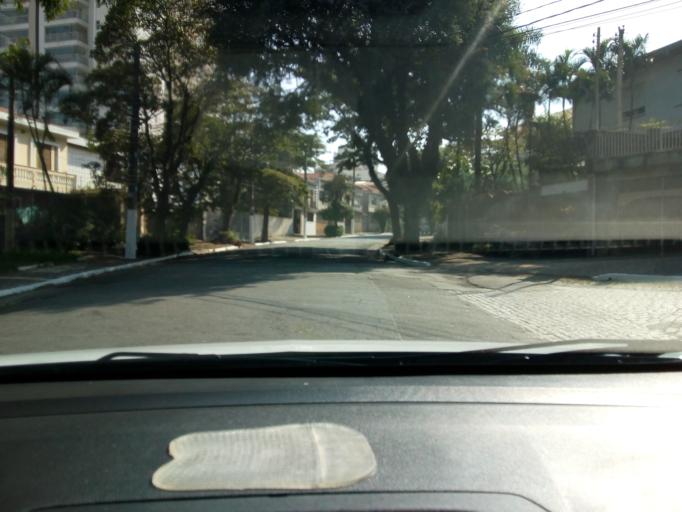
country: BR
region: Sao Paulo
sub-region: Sao Paulo
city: Sao Paulo
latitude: -23.5808
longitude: -46.6189
